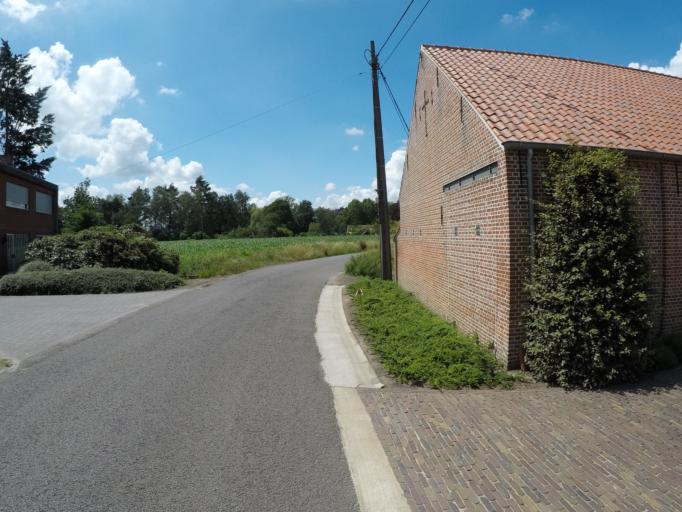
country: BE
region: Flanders
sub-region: Provincie Antwerpen
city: Vosselaar
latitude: 51.2649
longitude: 4.8770
